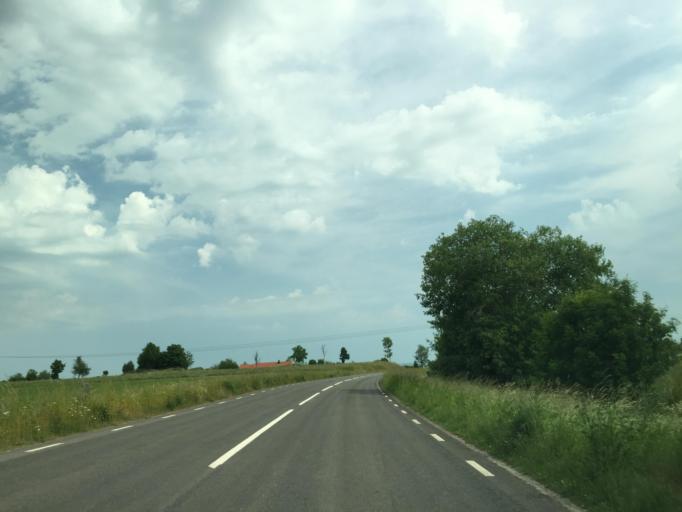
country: SE
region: Vaestra Goetaland
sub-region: Skovde Kommun
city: Skultorp
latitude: 58.3298
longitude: 13.7915
